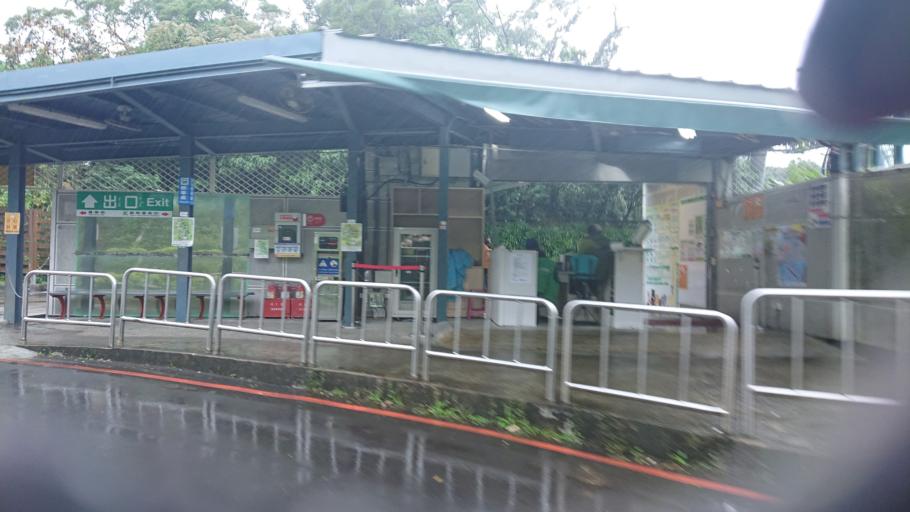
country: TW
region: Taipei
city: Taipei
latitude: 24.9900
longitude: 121.5873
